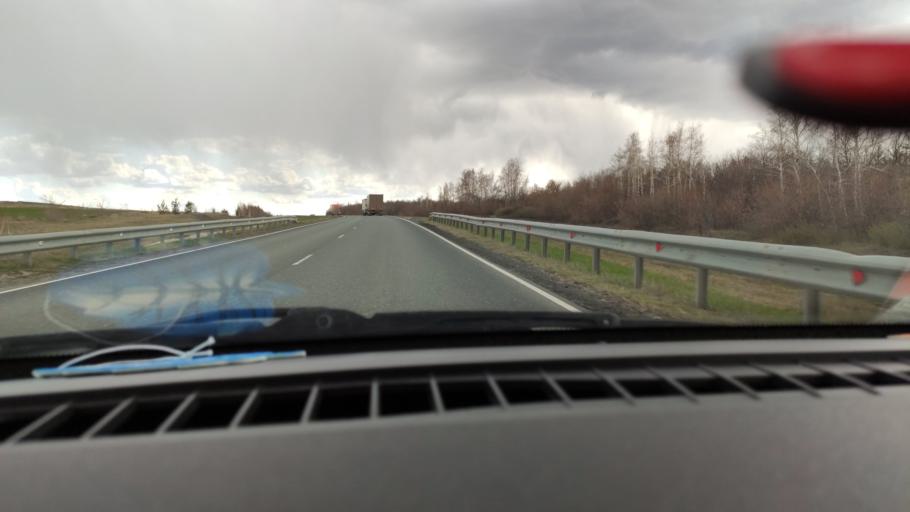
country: RU
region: Saratov
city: Balakovo
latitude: 52.1647
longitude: 47.8248
